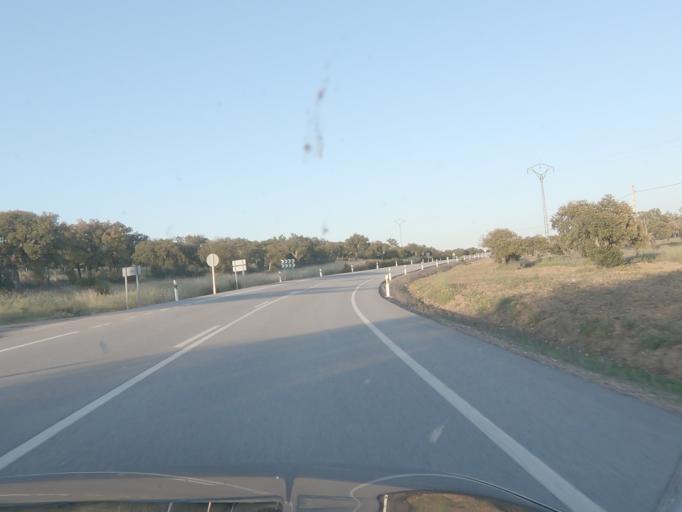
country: ES
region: Extremadura
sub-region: Provincia de Caceres
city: Carbajo
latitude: 39.5071
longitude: -7.1470
